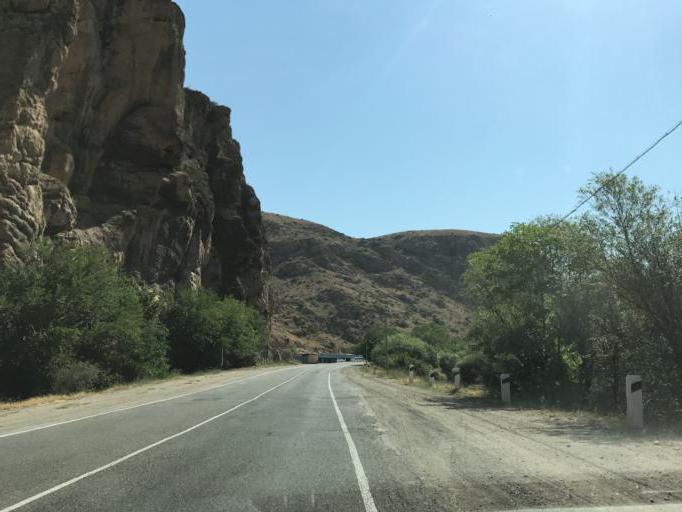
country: AM
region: Vayots' Dzori Marz
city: Areni
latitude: 39.7325
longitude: 45.2047
